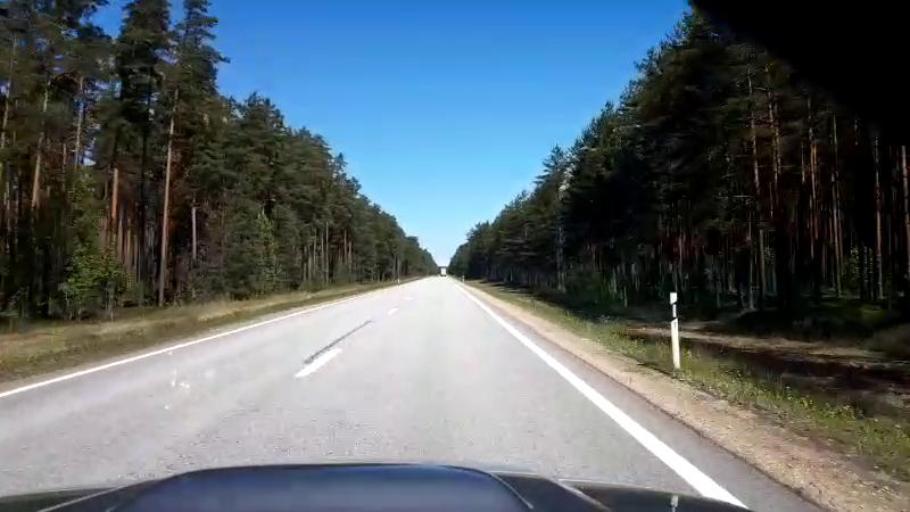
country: LV
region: Salacgrivas
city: Salacgriva
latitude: 57.5569
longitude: 24.4335
